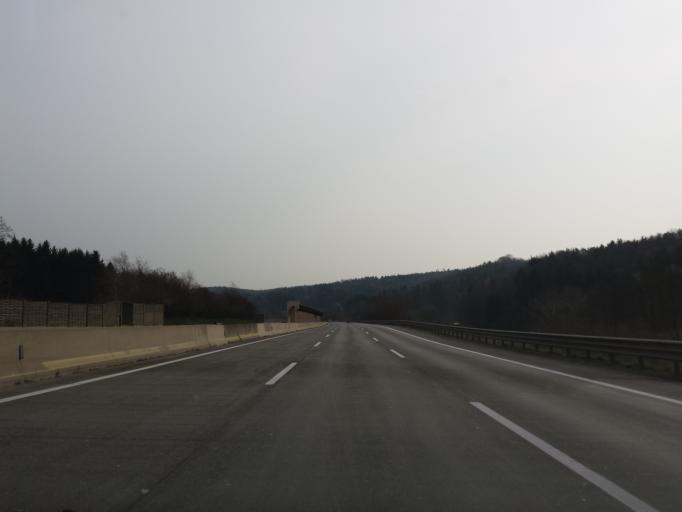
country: AT
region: Styria
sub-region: Politischer Bezirk Graz-Umgebung
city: Nestelbach bei Graz
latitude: 47.0688
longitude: 15.6282
